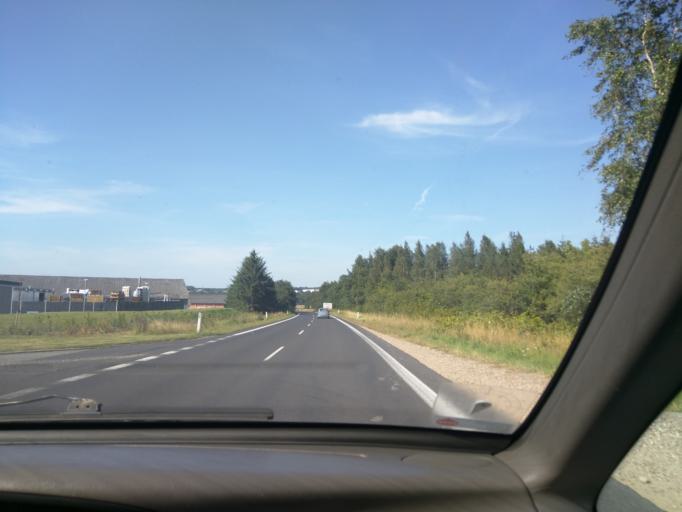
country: DK
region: Central Jutland
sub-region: Viborg Kommune
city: Bjerringbro
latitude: 56.3668
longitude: 9.6764
